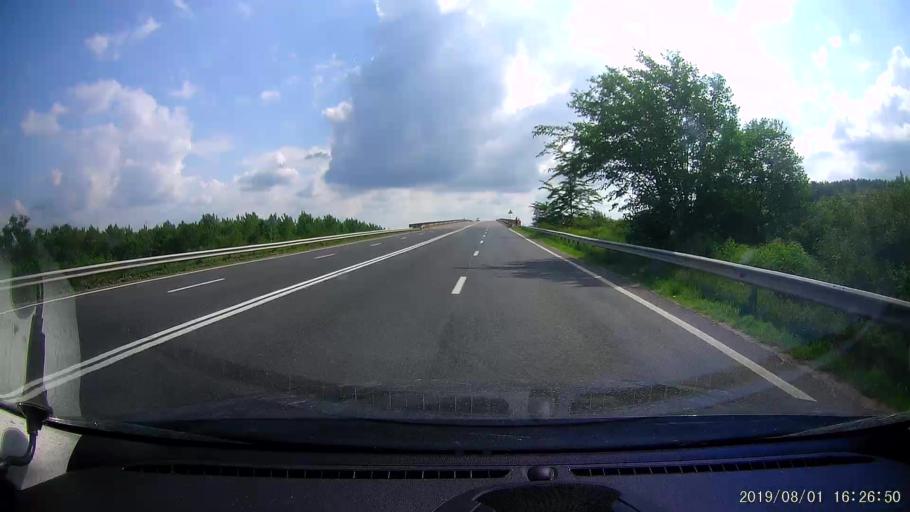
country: RO
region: Calarasi
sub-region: Municipiul Calarasi
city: Calarasi
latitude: 44.1720
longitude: 27.3173
